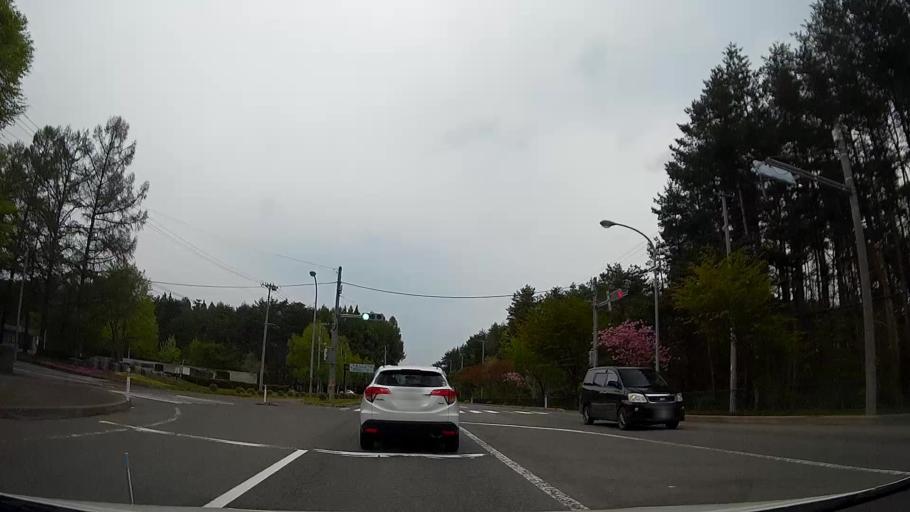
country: JP
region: Aomori
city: Aomori Shi
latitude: 40.7535
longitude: 140.7759
